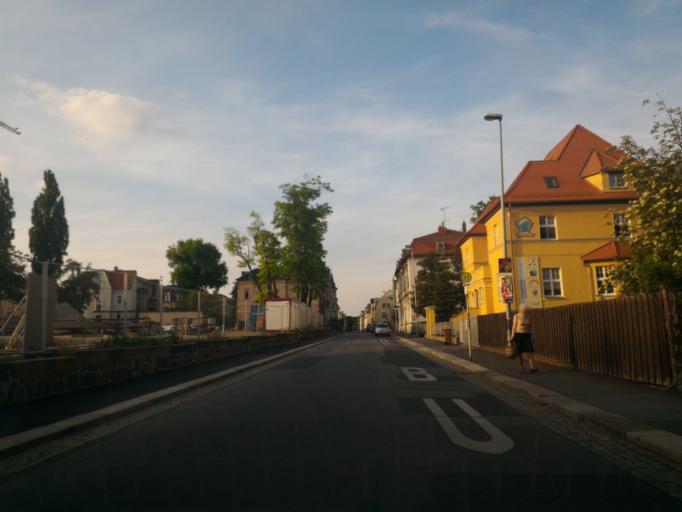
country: DE
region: Saxony
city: Zittau
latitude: 50.8987
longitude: 14.8102
